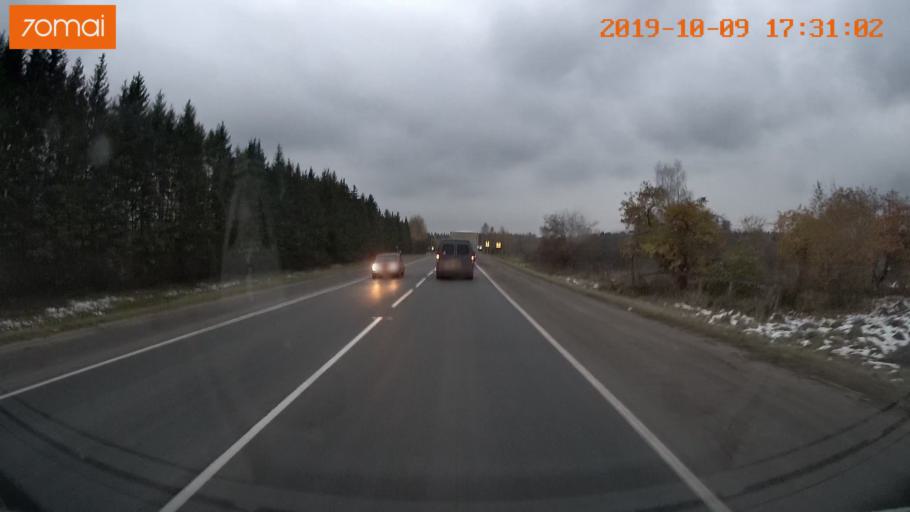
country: RU
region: Ivanovo
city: Bogorodskoye
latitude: 57.1382
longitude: 41.0431
